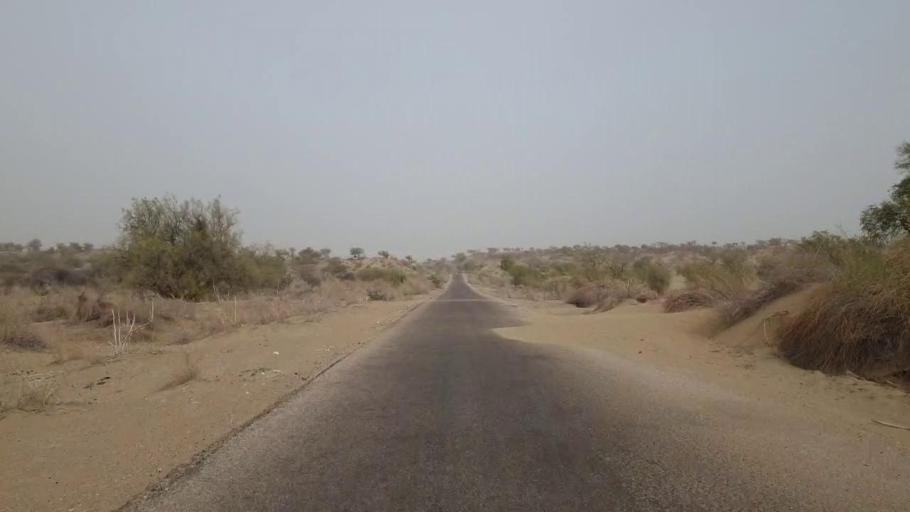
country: PK
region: Sindh
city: Islamkot
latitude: 24.5894
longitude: 70.2899
